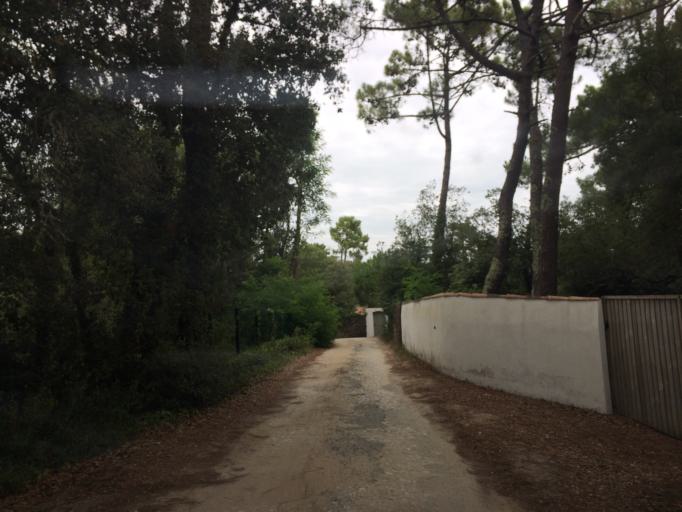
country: FR
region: Poitou-Charentes
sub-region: Departement de la Charente-Maritime
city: La Couarde-sur-Mer
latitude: 46.1999
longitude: -1.4497
